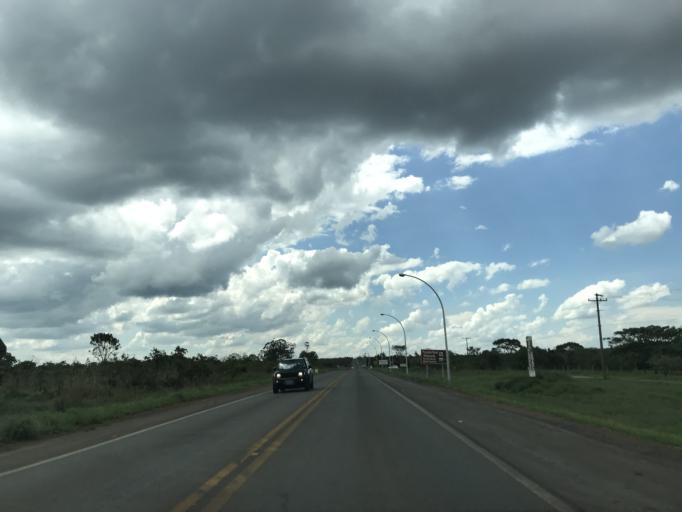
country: BR
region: Federal District
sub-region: Brasilia
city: Brasilia
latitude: -15.6847
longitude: -47.8638
